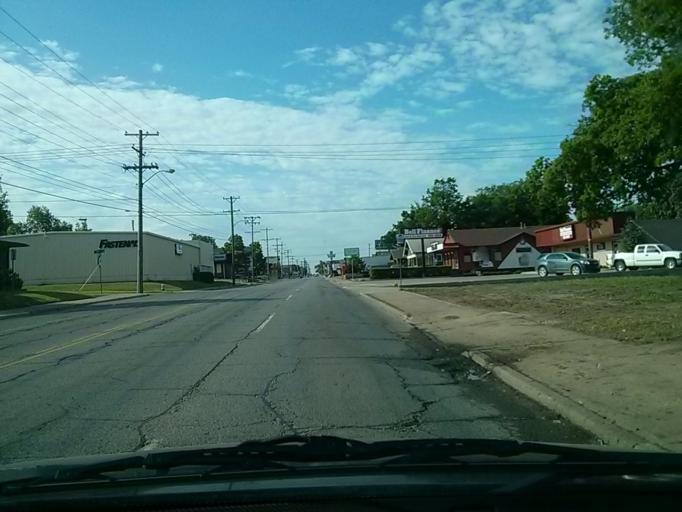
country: US
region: Oklahoma
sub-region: Tulsa County
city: Tulsa
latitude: 36.1464
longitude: -95.9757
